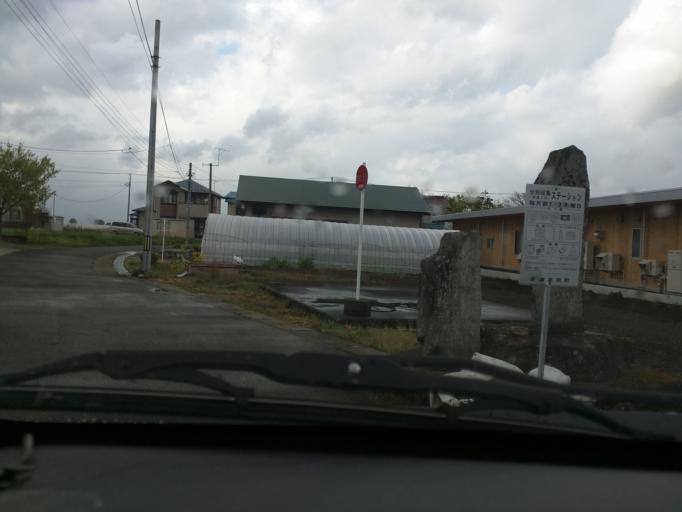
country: JP
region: Fukushima
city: Kitakata
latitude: 37.4454
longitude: 139.8537
